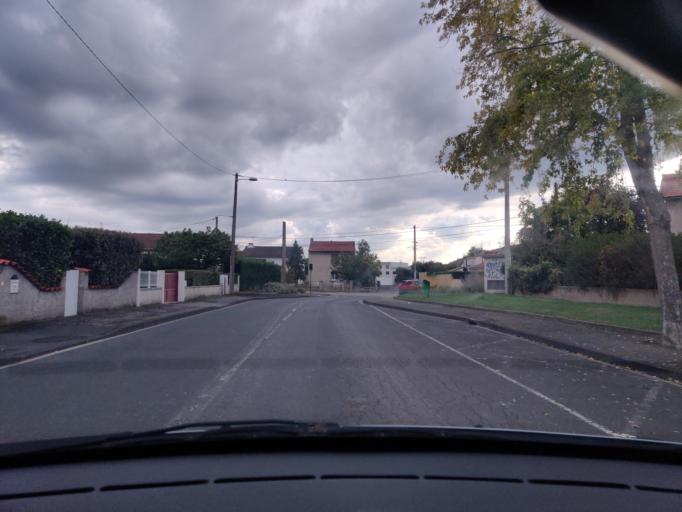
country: FR
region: Auvergne
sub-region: Departement du Puy-de-Dome
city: Menetrol
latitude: 45.8822
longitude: 3.1272
